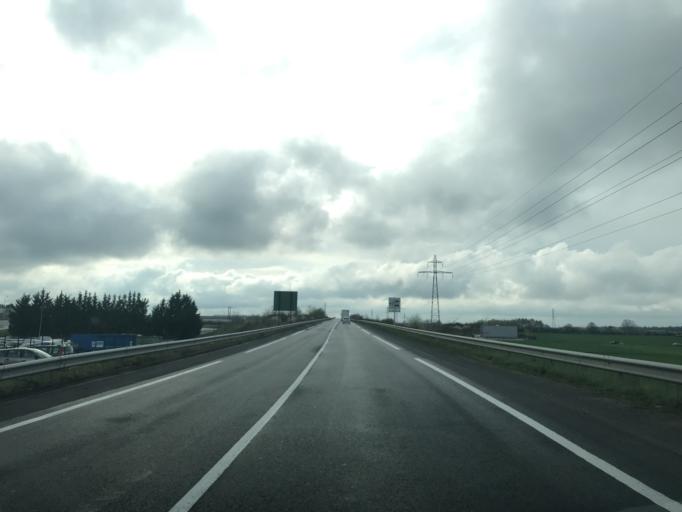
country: FR
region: Centre
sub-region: Departement du Loiret
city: Gien
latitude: 47.7102
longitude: 2.6401
